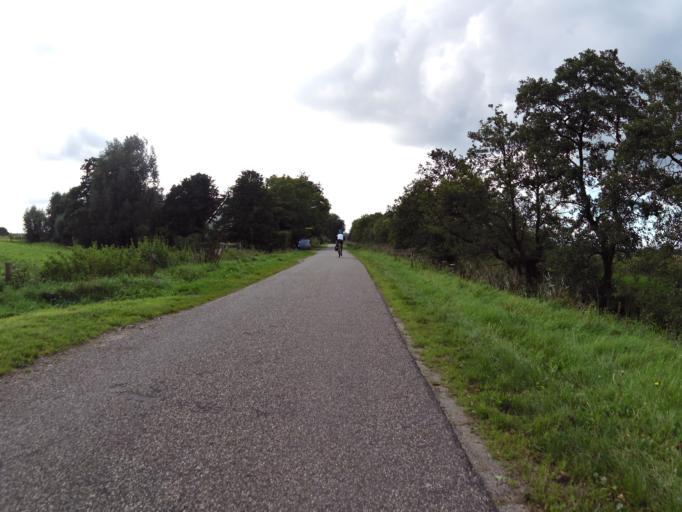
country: NL
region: North Holland
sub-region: Gemeente Wijdemeren
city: Nieuw-Loosdrecht
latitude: 52.1804
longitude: 5.1299
